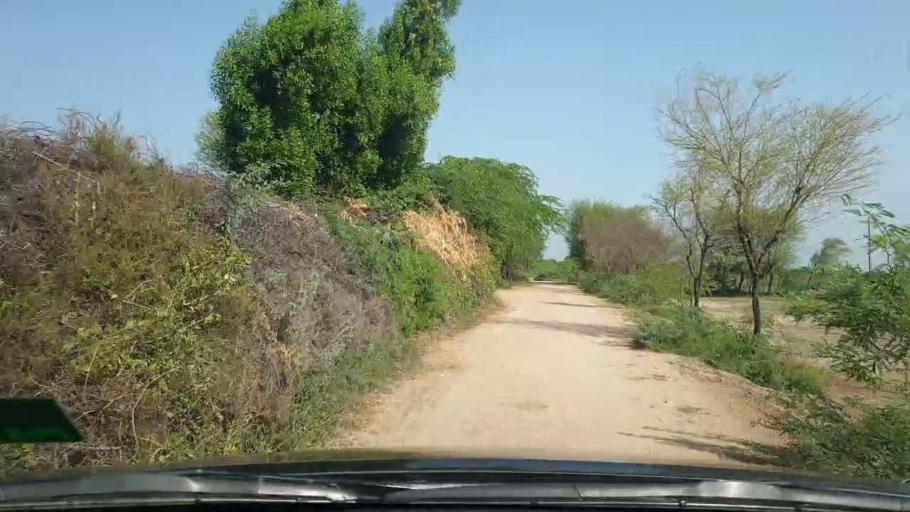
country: PK
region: Sindh
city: Tando Bago
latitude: 24.6860
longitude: 69.0096
